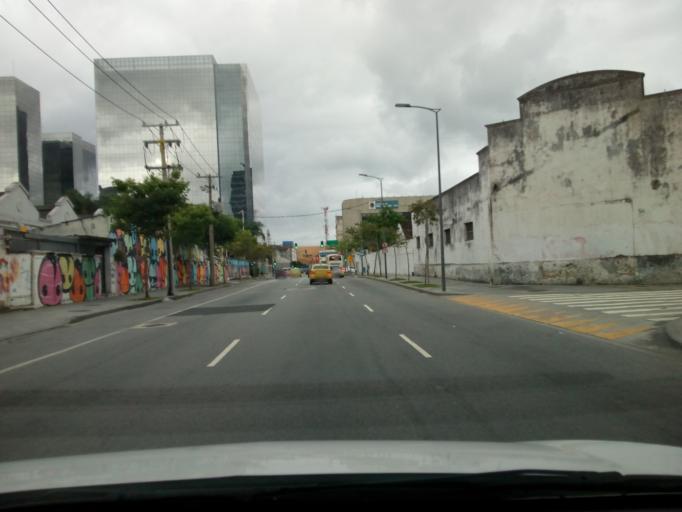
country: BR
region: Rio de Janeiro
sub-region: Rio De Janeiro
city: Rio de Janeiro
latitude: -22.8989
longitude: -43.2034
